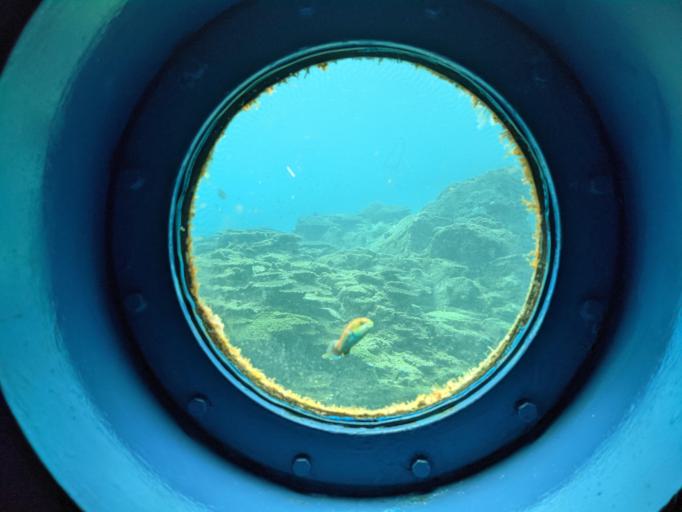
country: JP
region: Wakayama
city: Shingu
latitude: 33.4795
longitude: 135.7464
